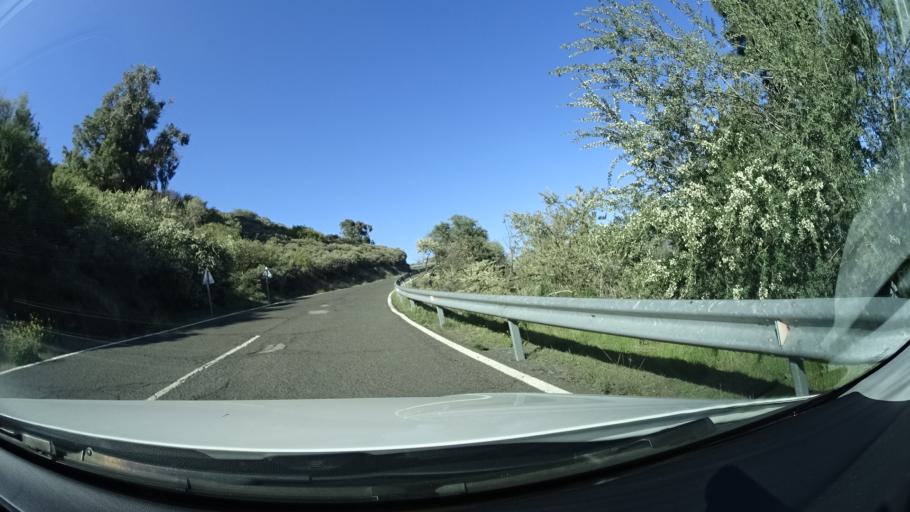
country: ES
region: Canary Islands
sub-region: Provincia de Las Palmas
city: San Bartolome
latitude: 27.9627
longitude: -15.5477
